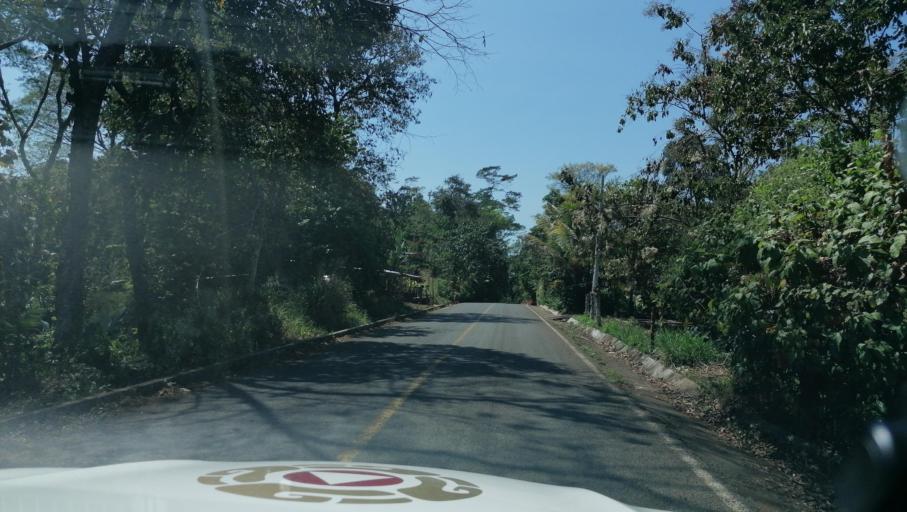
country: MX
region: Chiapas
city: Veinte de Noviembre
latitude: 15.0070
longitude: -92.2291
